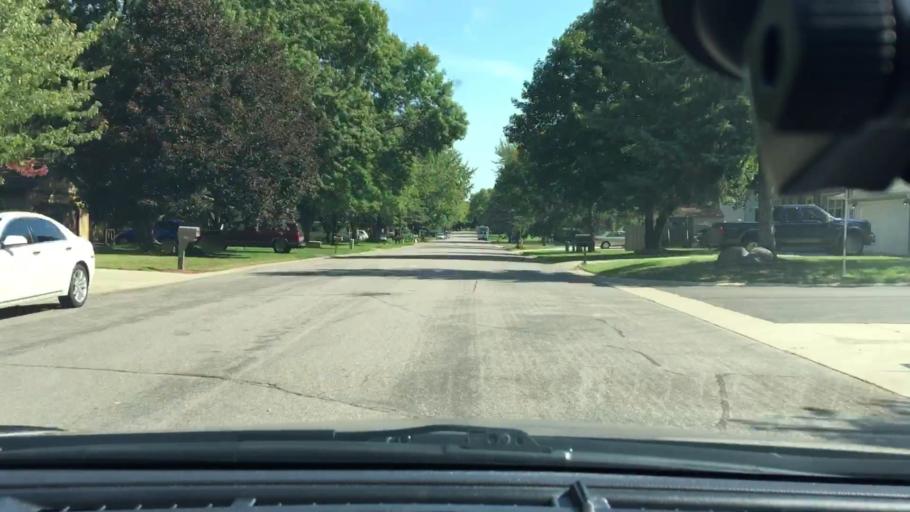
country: US
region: Minnesota
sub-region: Wright County
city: Saint Michael
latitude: 45.2024
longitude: -93.6735
